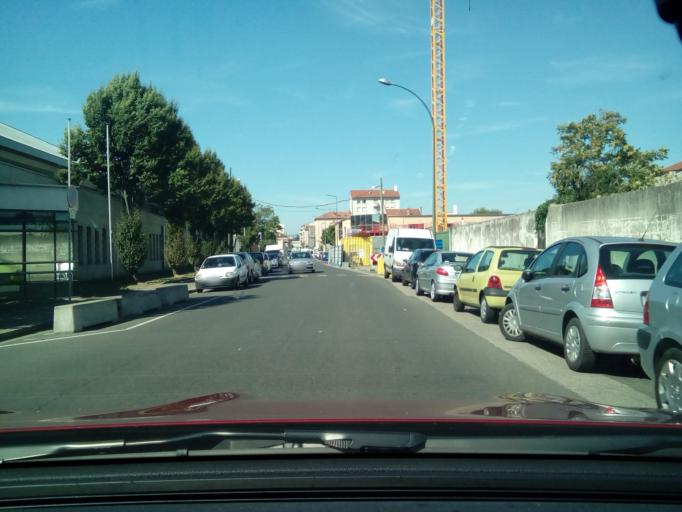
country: FR
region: Rhone-Alpes
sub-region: Departement du Rhone
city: Villeurbanne
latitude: 45.7583
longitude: 4.8983
